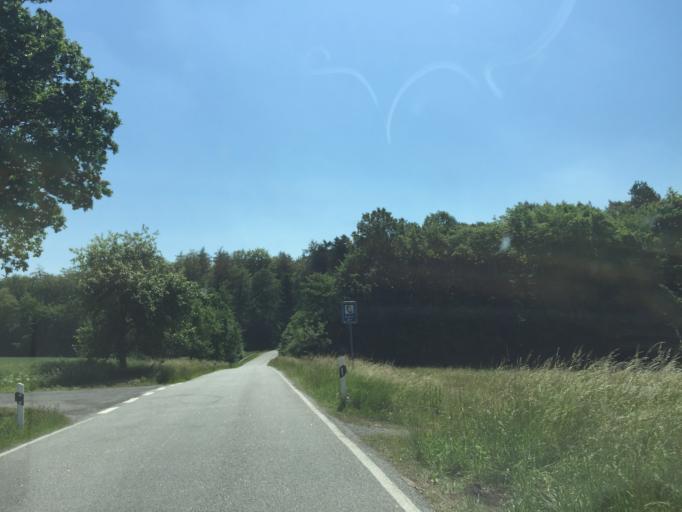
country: DE
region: Baden-Wuerttemberg
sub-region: Karlsruhe Region
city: Walldurn
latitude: 49.6086
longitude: 9.3440
